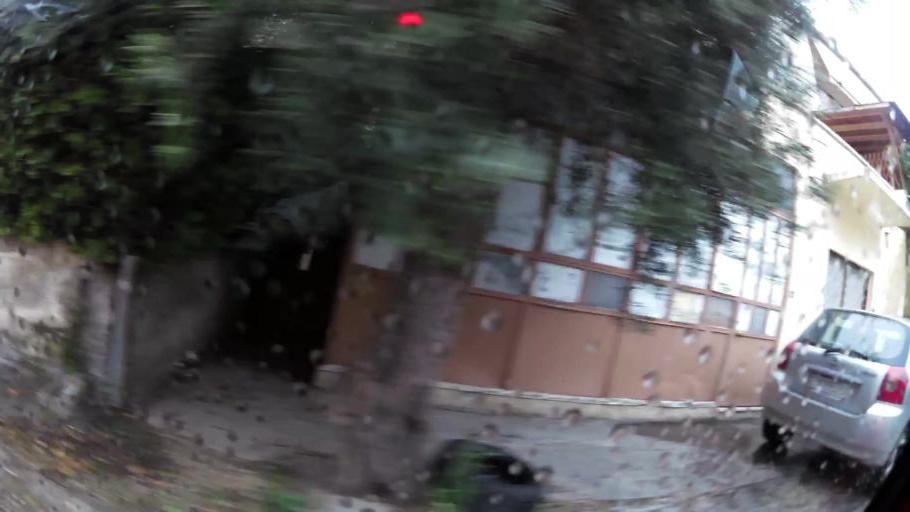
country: GR
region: Attica
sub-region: Nomarchia Athinas
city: Nea Filadelfeia
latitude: 38.0375
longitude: 23.7317
